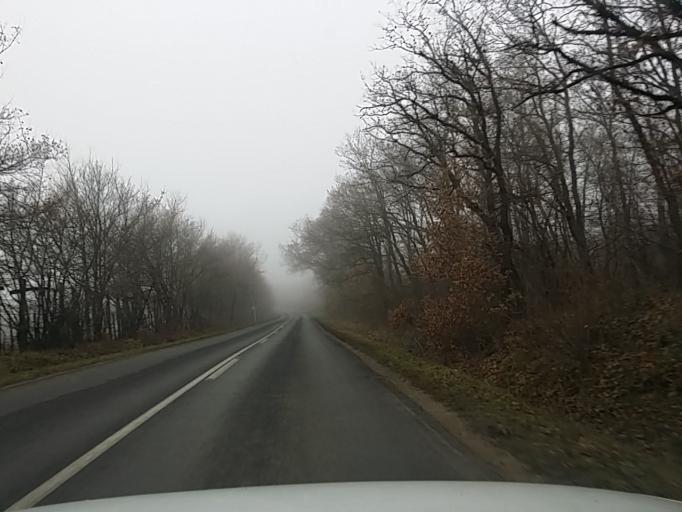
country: HU
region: Pest
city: Budakeszi
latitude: 47.5234
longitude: 18.9007
